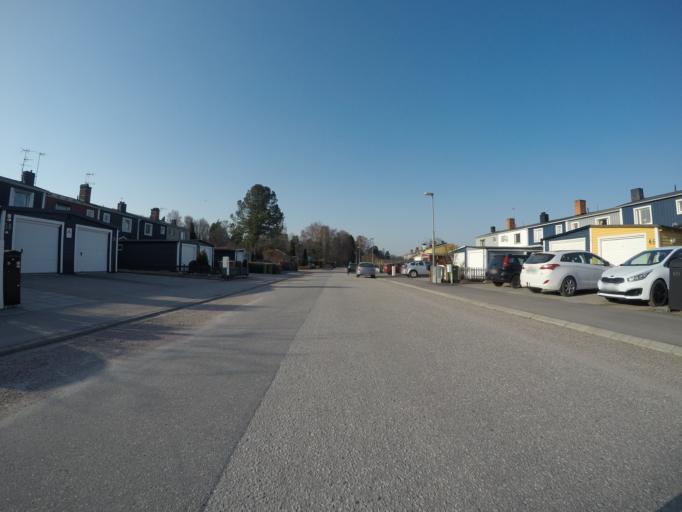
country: SE
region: Vaestmanland
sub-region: Kungsors Kommun
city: Kungsoer
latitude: 59.4213
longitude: 16.1127
